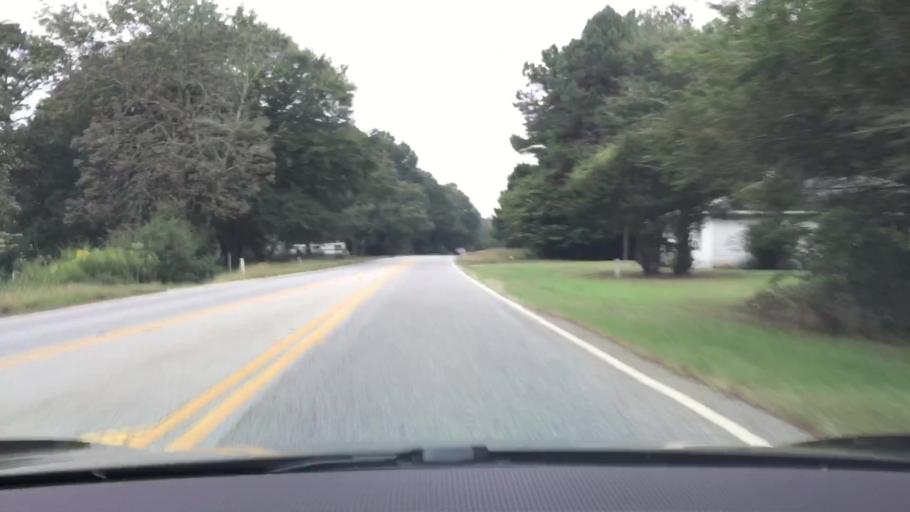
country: US
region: Georgia
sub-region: Barrow County
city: Russell
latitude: 33.9626
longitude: -83.6730
